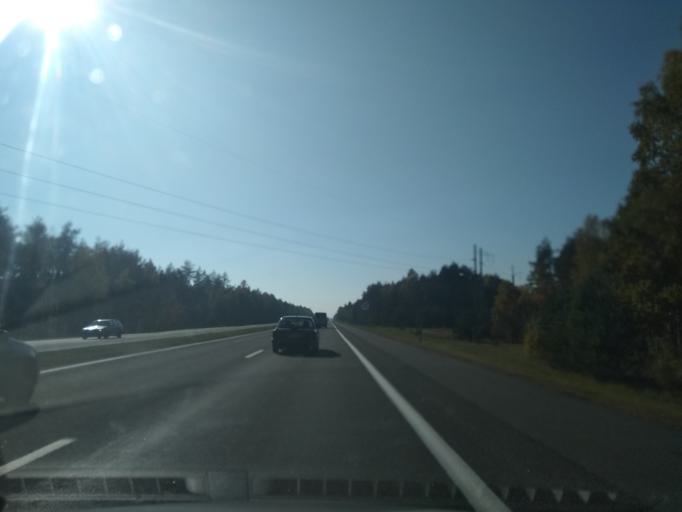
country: BY
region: Brest
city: Ivatsevichy
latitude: 52.8062
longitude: 25.5732
